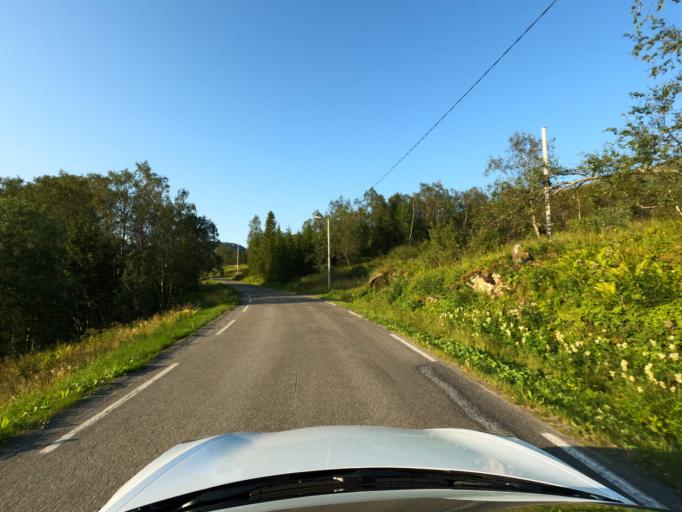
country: NO
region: Nordland
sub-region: Ballangen
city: Ballangen
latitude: 68.5240
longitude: 16.7649
